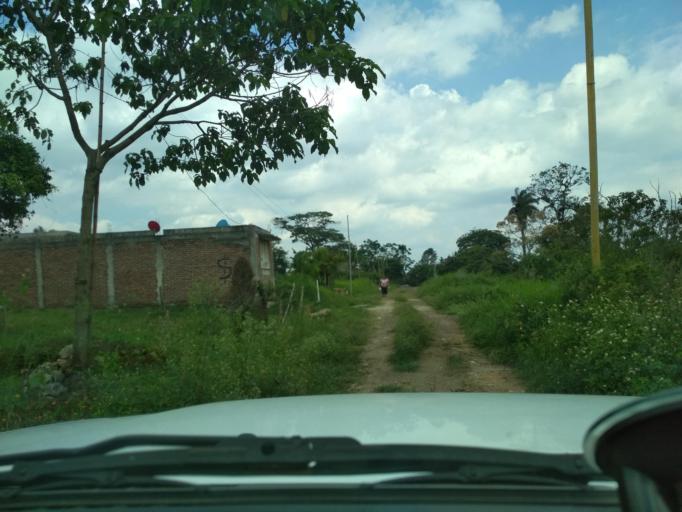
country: MX
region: Veracruz
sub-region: Fortin
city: Monte Salas
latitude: 18.9352
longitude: -97.0131
